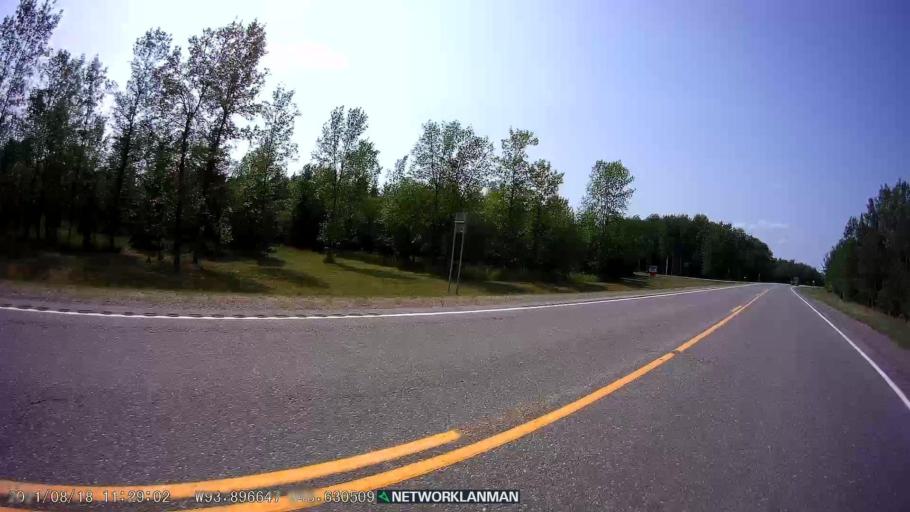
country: US
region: Minnesota
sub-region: Koochiching County
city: International Falls
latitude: 48.6306
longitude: -93.8974
